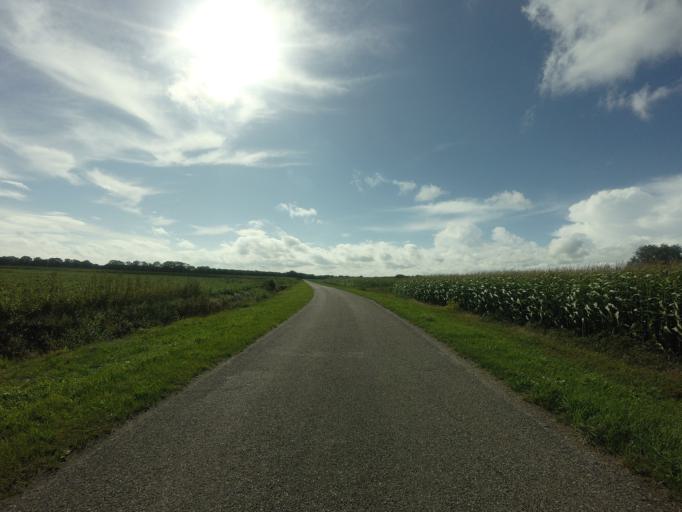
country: NL
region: Groningen
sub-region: Gemeente Leek
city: Leek
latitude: 53.0182
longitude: 6.3057
